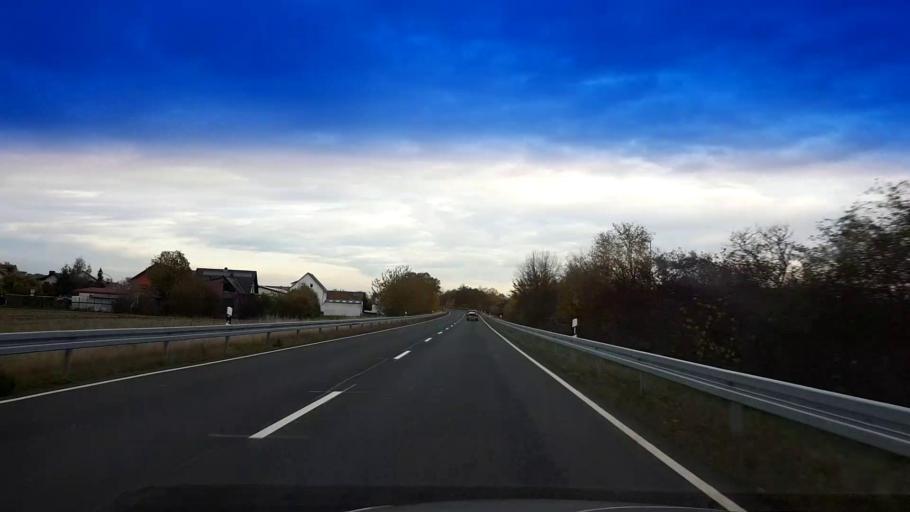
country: DE
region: Bavaria
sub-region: Upper Franconia
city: Viereth-Trunstadt
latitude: 49.9317
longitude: 10.7433
